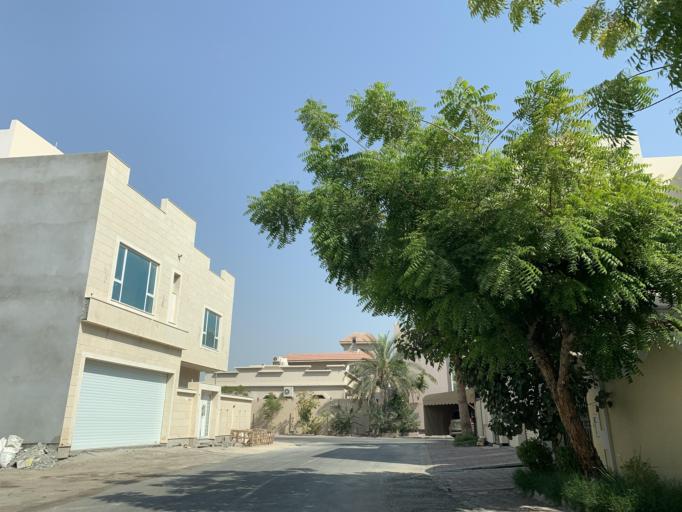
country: BH
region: Northern
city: Madinat `Isa
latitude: 26.1915
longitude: 50.5098
